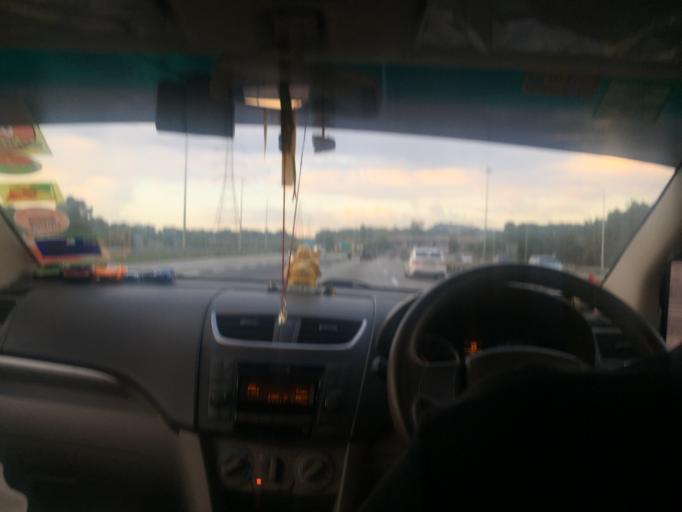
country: MY
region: Selangor
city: Subang Jaya
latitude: 2.9816
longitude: 101.5717
